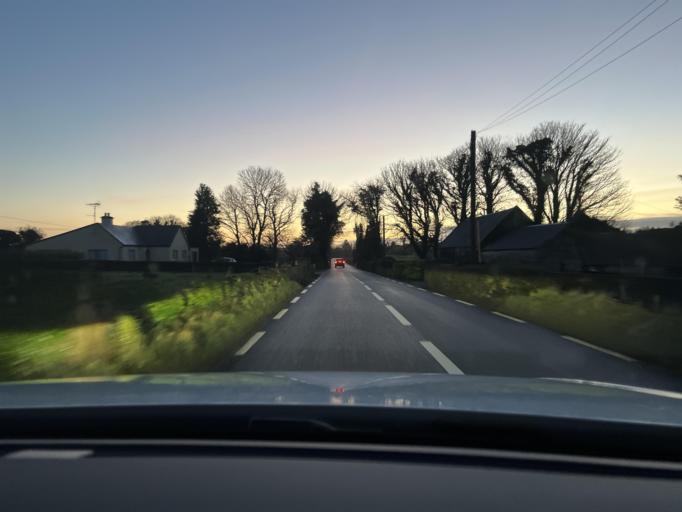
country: IE
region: Connaught
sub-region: County Leitrim
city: Carrick-on-Shannon
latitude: 53.9935
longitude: -8.0345
